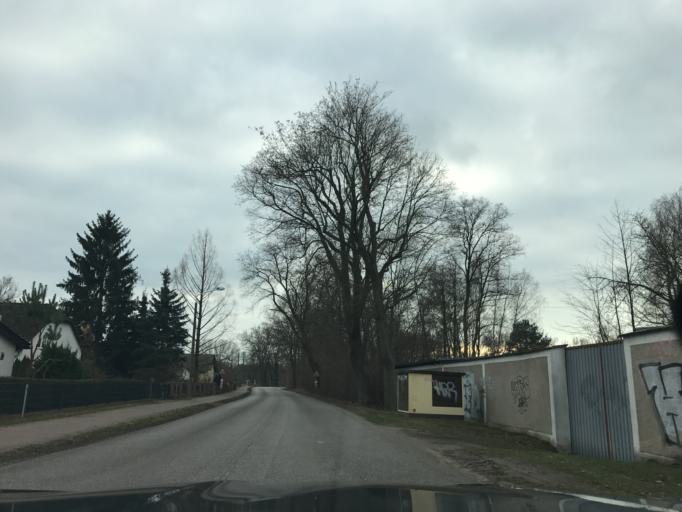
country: DE
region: Brandenburg
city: Brandenburg an der Havel
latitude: 52.3743
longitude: 12.5461
